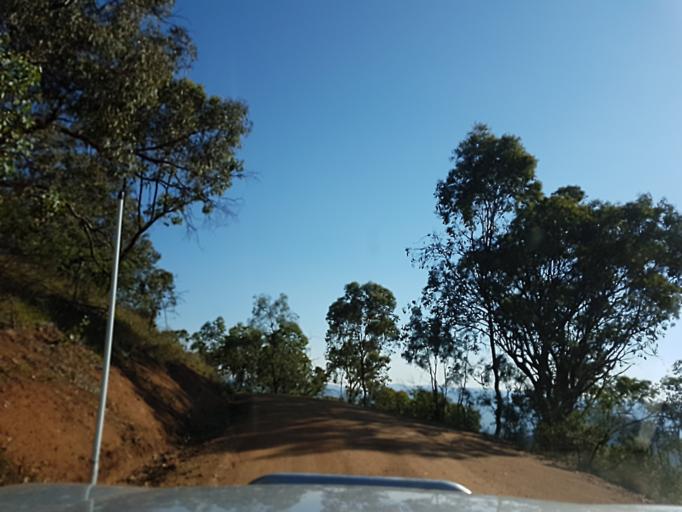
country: AU
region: New South Wales
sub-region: Snowy River
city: Jindabyne
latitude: -36.9454
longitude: 148.3476
